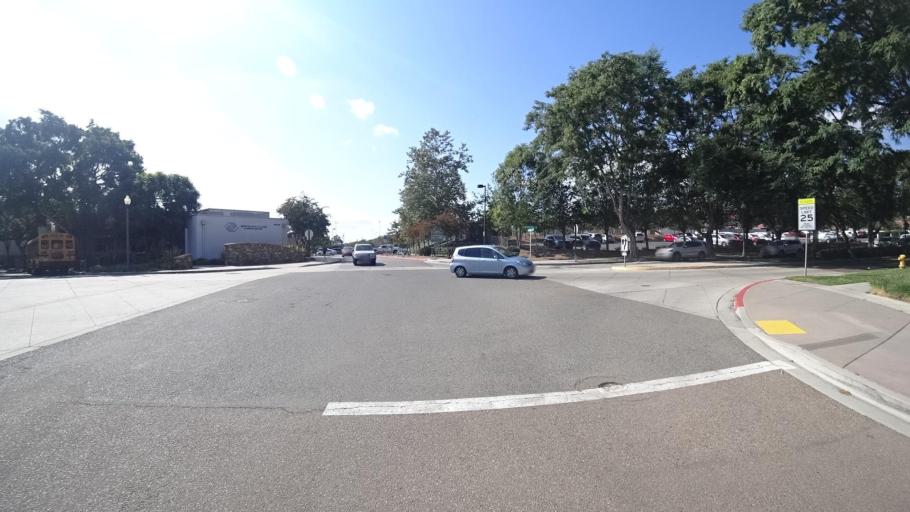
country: US
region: California
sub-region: San Diego County
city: Fairbanks Ranch
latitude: 33.0040
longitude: -117.1157
